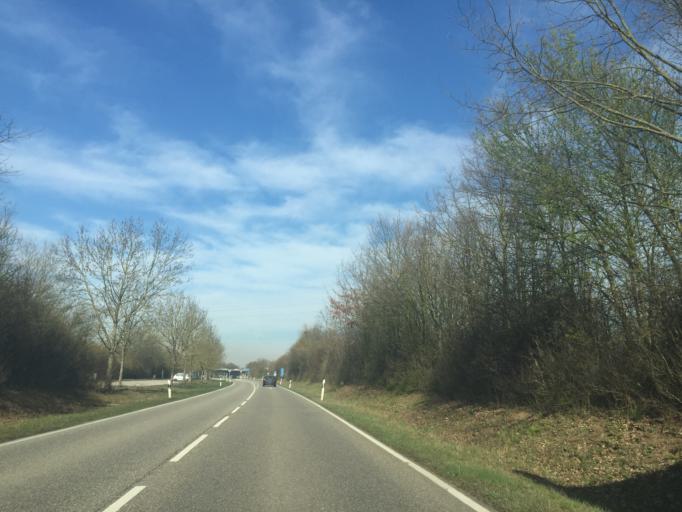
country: DE
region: Baden-Wuerttemberg
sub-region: Karlsruhe Region
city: Dossenheim
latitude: 49.4469
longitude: 8.6530
